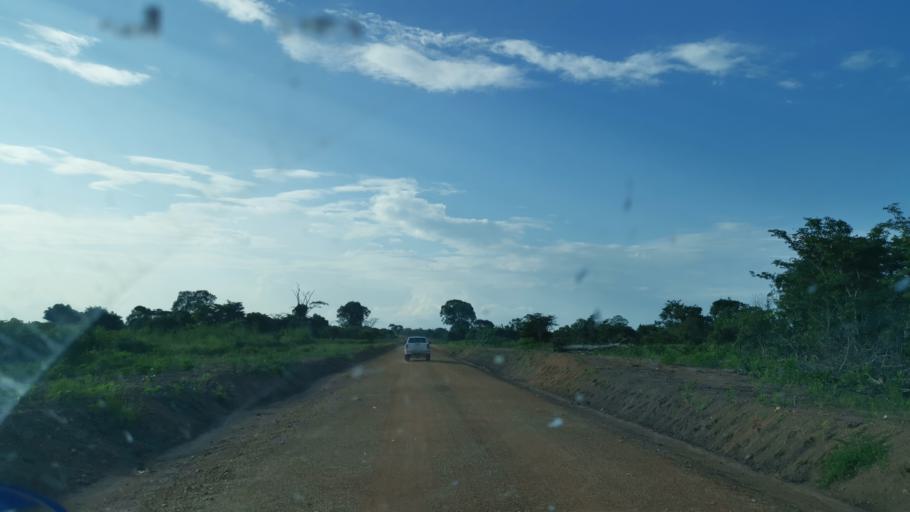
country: ZM
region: Luapula
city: Samfya
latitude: -11.1122
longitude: 29.5768
